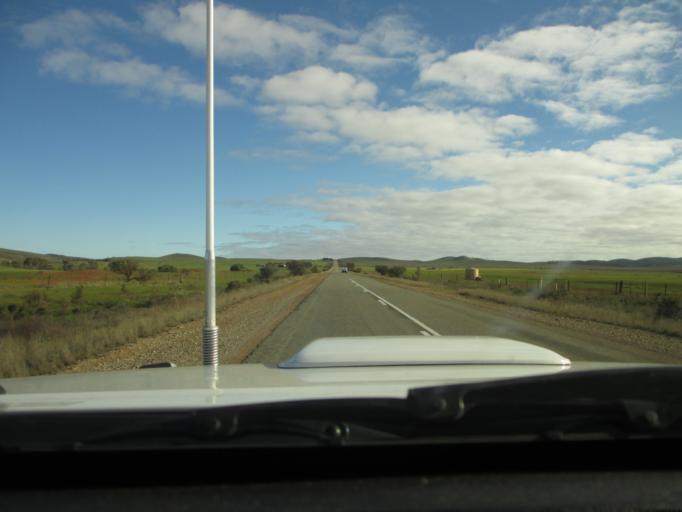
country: AU
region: South Australia
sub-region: Peterborough
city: Peterborough
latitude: -32.6330
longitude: 138.5936
